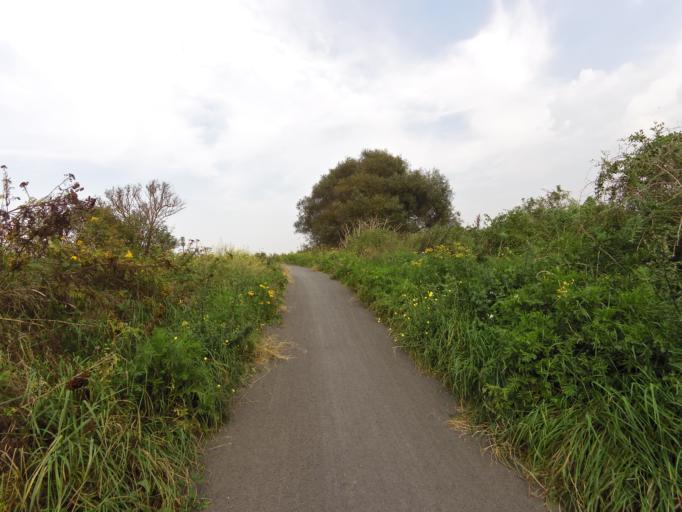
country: BE
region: Flanders
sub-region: Provincie West-Vlaanderen
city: Ostend
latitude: 51.1986
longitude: 2.9510
